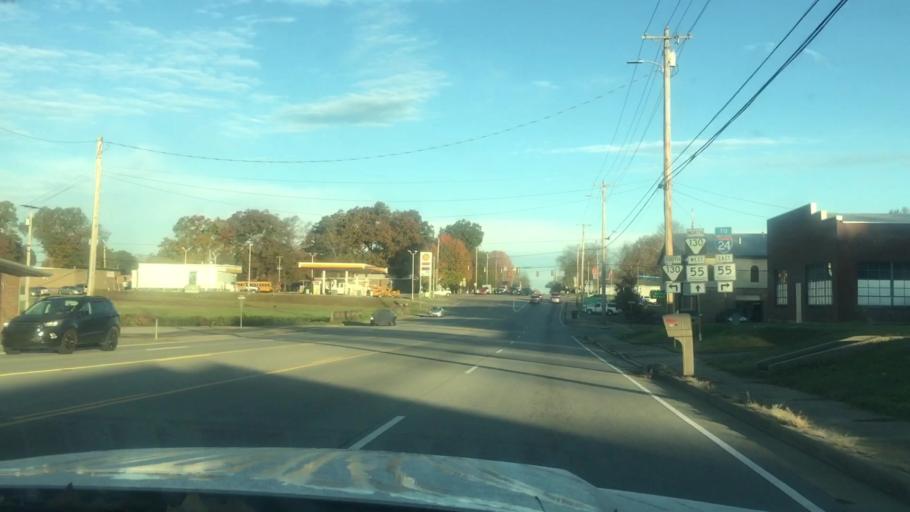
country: US
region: Tennessee
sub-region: Coffee County
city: Tullahoma
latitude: 35.3545
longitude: -86.2048
